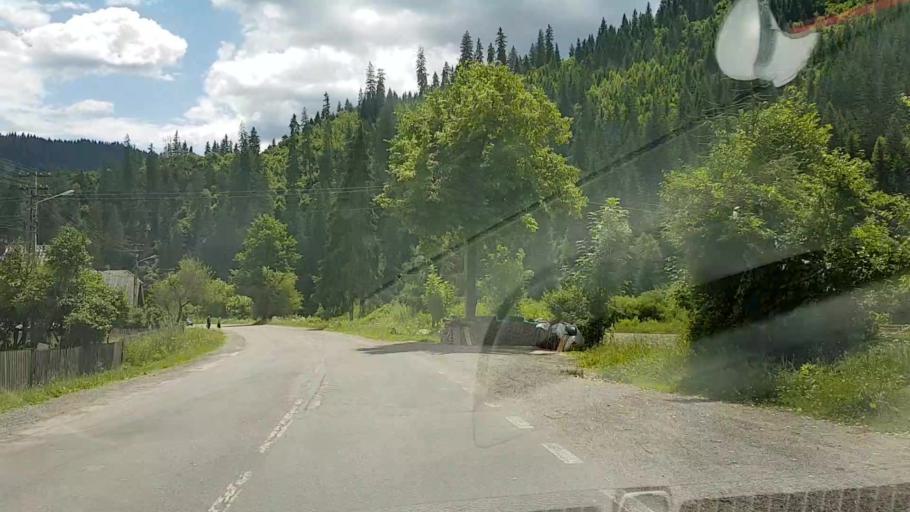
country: RO
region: Suceava
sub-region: Comuna Brosteni
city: Brosteni
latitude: 47.2401
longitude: 25.6911
